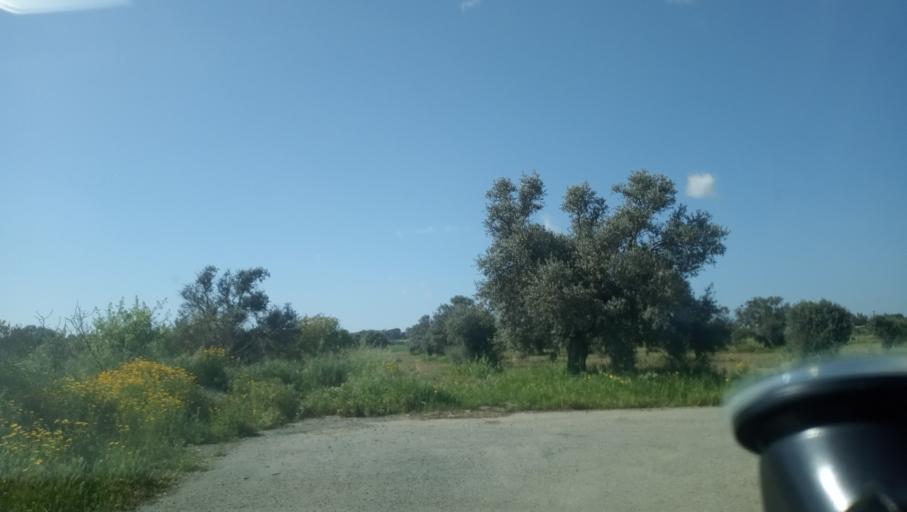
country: CY
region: Lefkosia
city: Tseri
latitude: 35.0899
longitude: 33.3094
